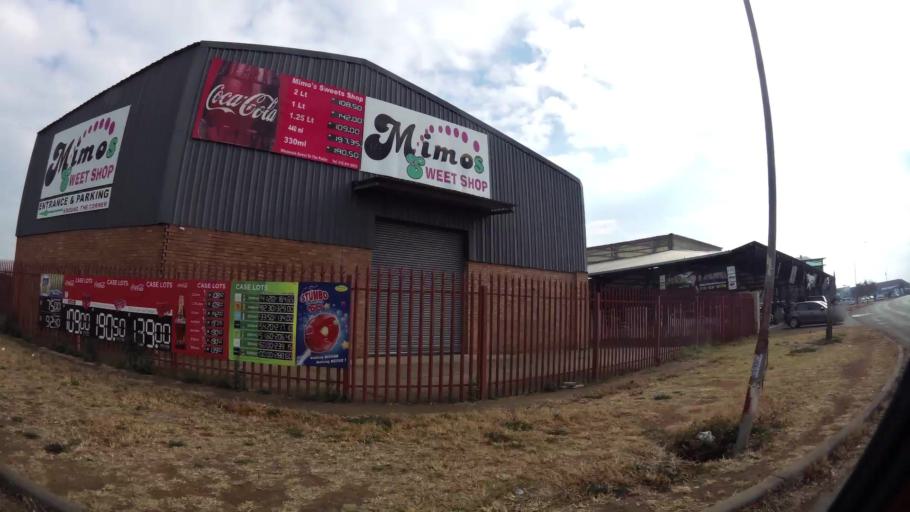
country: ZA
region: Gauteng
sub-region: Sedibeng District Municipality
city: Vanderbijlpark
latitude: -26.6961
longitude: 27.8326
